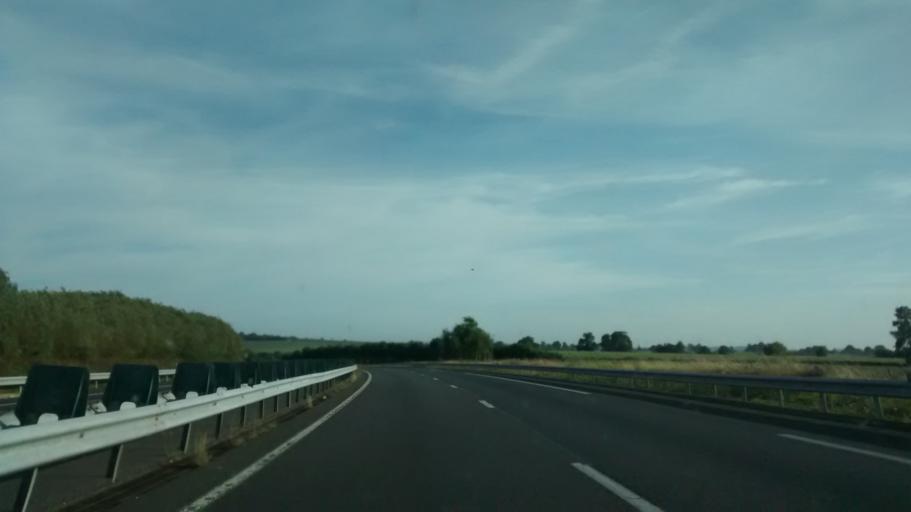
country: FR
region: Lower Normandy
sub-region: Departement de la Manche
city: Villedieu-les-Poeles
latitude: 48.8420
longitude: -1.2494
